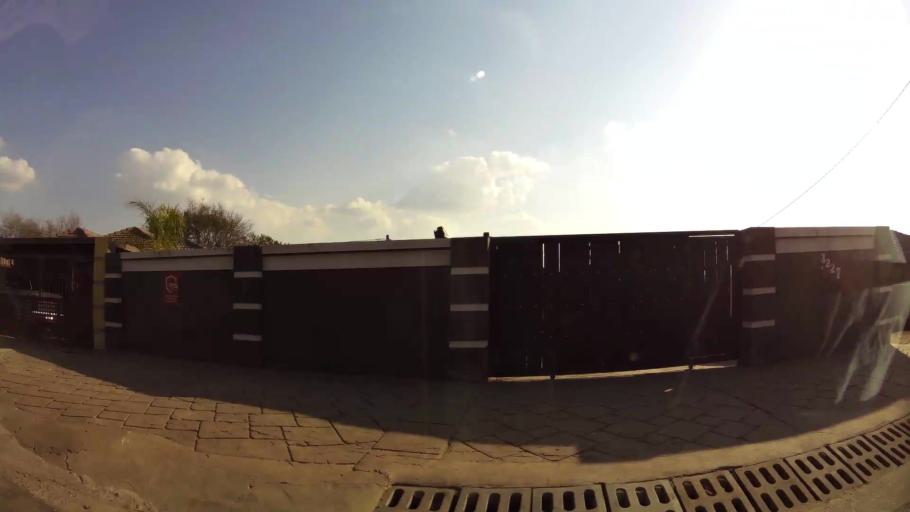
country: ZA
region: Gauteng
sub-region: Ekurhuleni Metropolitan Municipality
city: Tembisa
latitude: -25.9530
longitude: 28.2107
